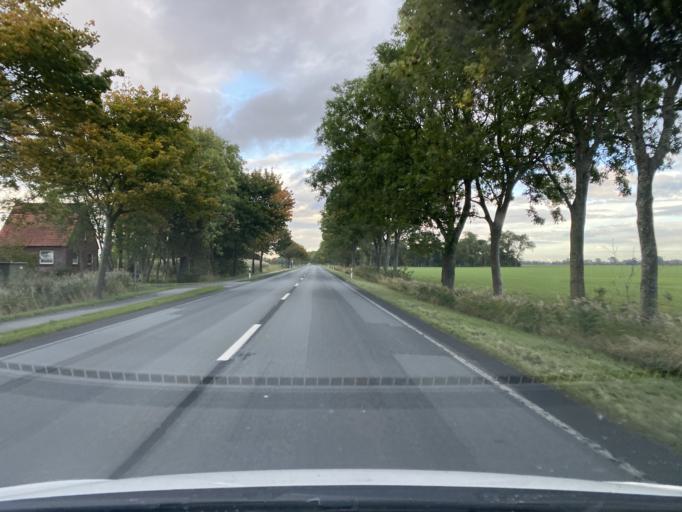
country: DE
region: Lower Saxony
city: Nordleda
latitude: 53.8016
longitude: 8.8282
